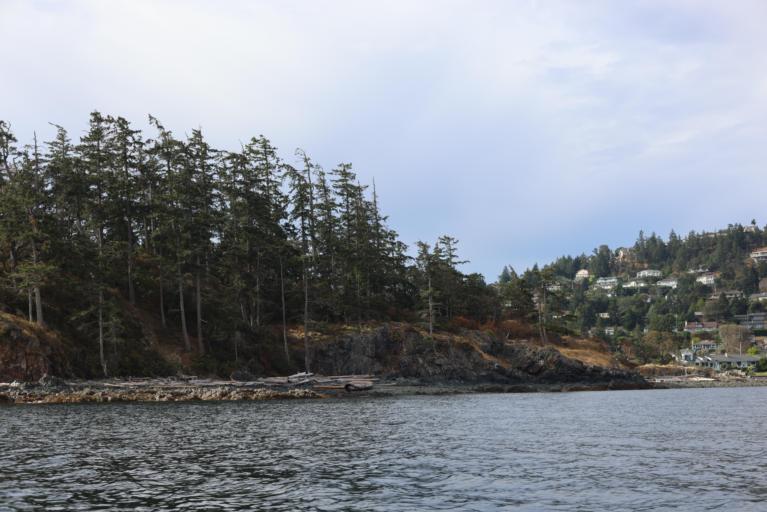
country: CA
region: British Columbia
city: Nanaimo
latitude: 49.2303
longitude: -123.9505
